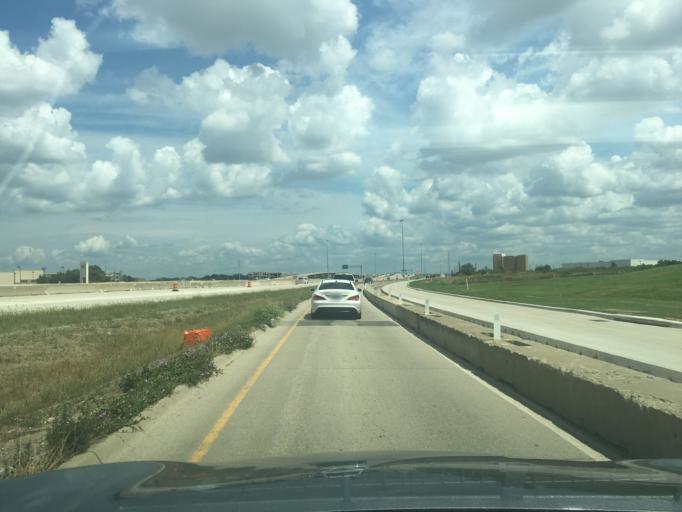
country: US
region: Texas
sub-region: Dallas County
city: Coppell
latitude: 32.9653
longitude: -97.0348
